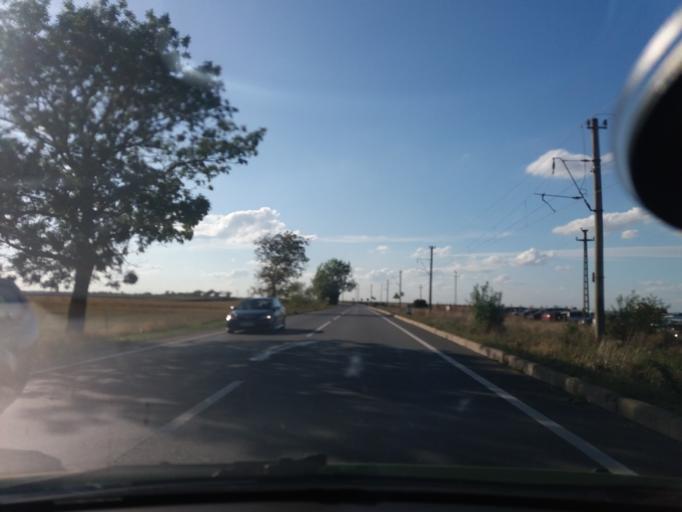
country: RO
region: Arad
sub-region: Comuna Paulis
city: Sambateni
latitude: 46.1441
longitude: 21.5140
